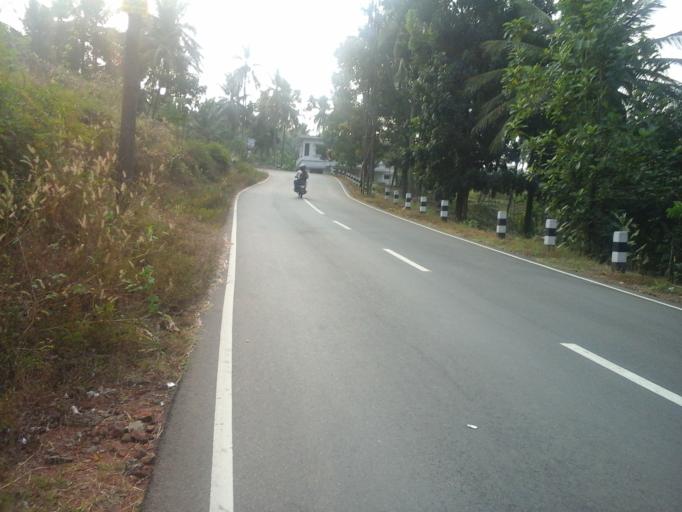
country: IN
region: Kerala
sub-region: Kannur
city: Taliparamba
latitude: 12.1442
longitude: 75.4391
